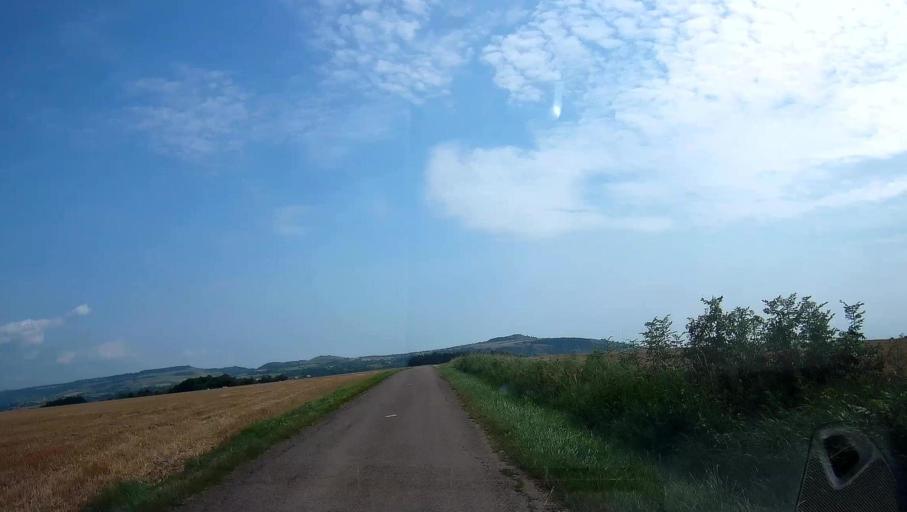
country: FR
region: Bourgogne
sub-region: Departement de la Cote-d'Or
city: Nolay
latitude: 46.8993
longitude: 4.6258
